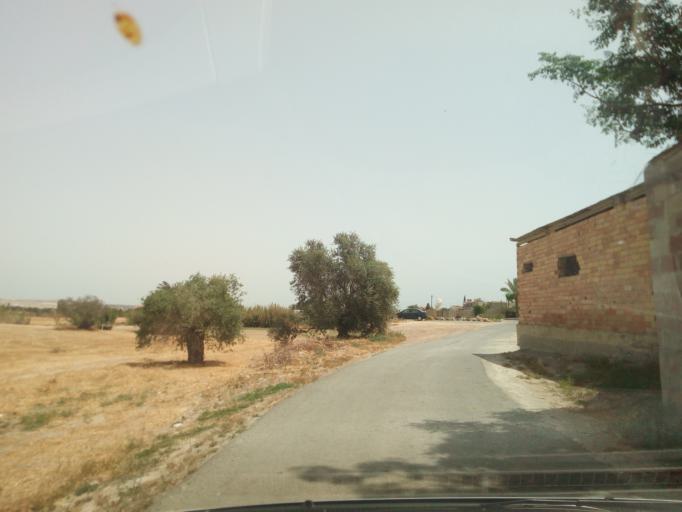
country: CY
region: Larnaka
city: Aradippou
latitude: 34.9547
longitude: 33.5889
